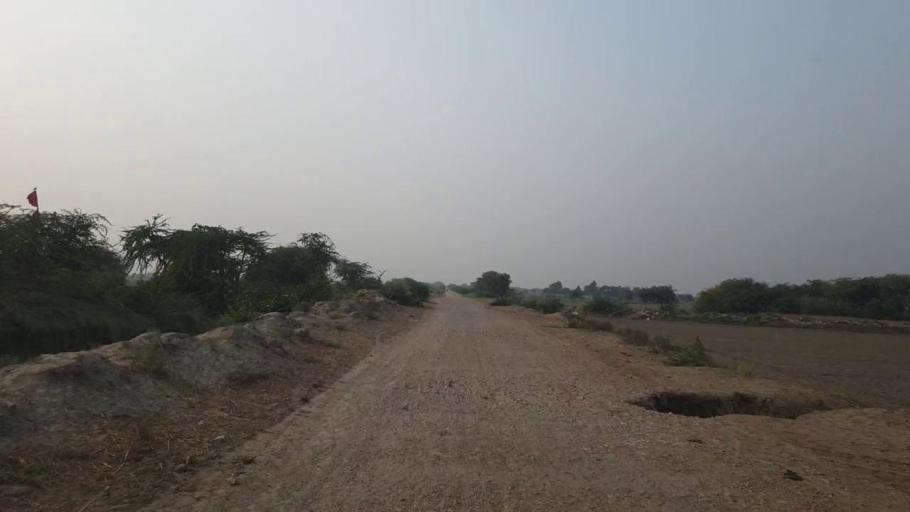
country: PK
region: Sindh
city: Mirpur Batoro
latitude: 24.6447
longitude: 68.3939
